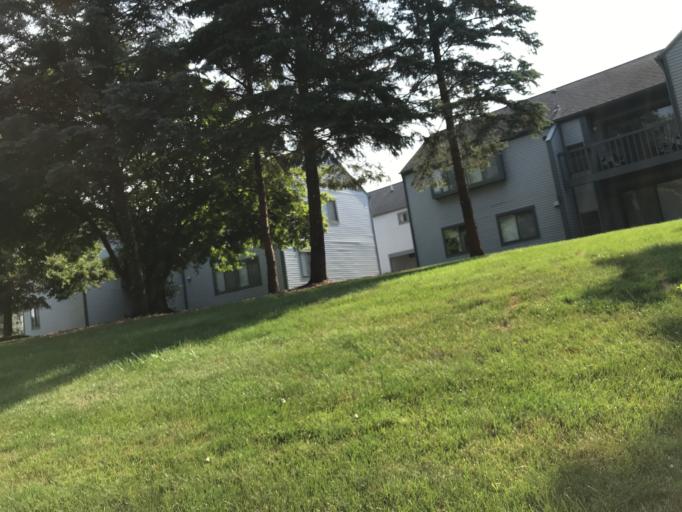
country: US
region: Michigan
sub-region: Washtenaw County
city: Ann Arbor
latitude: 42.2423
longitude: -83.7162
